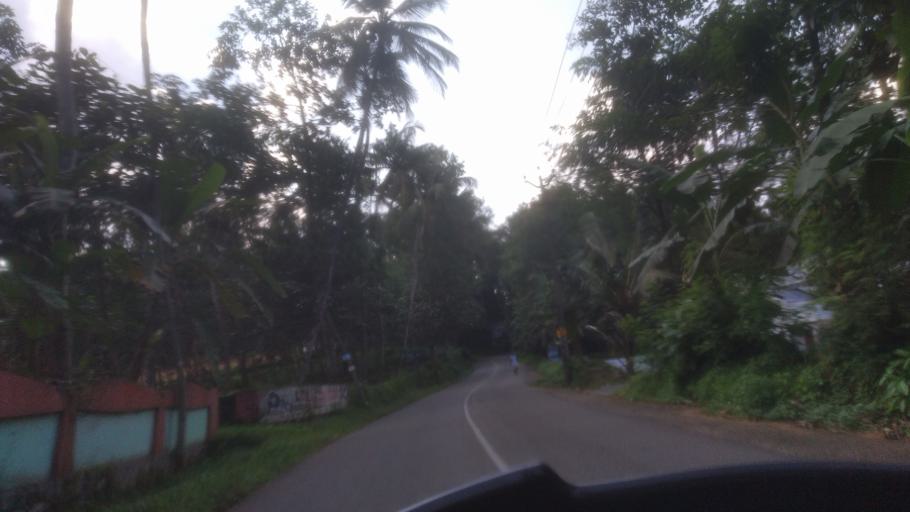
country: IN
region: Kerala
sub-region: Ernakulam
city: Kotamangalam
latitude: 10.0057
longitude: 76.6771
